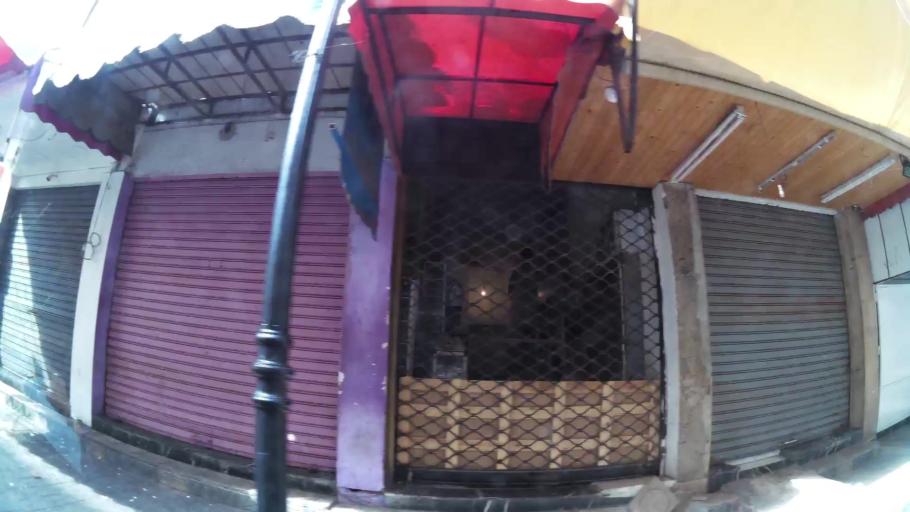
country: MA
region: Gharb-Chrarda-Beni Hssen
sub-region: Kenitra Province
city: Kenitra
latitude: 34.2637
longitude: -6.5635
